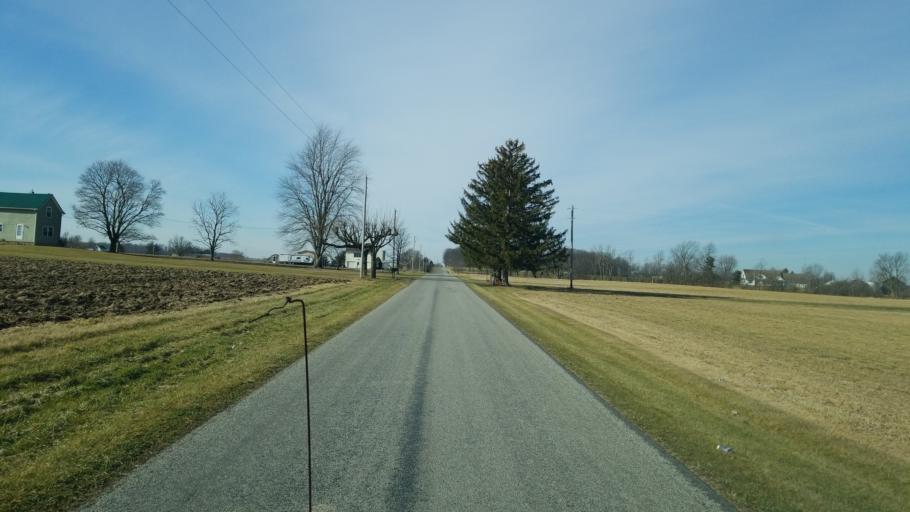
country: US
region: Ohio
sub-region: Hardin County
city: Ada
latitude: 40.8125
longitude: -83.8896
